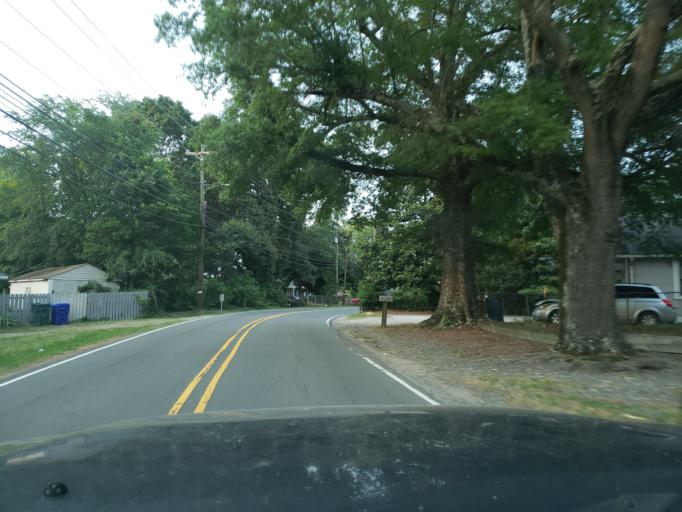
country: US
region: North Carolina
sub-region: Durham County
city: Durham
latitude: 35.9641
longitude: -78.8543
